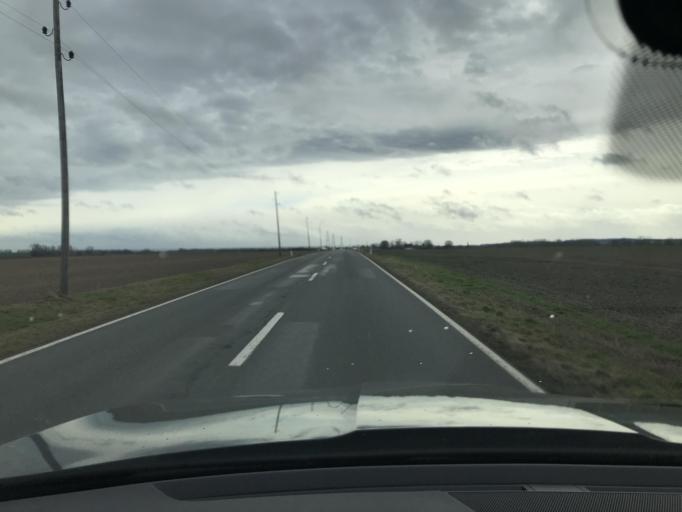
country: DE
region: Saxony-Anhalt
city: Wegeleben
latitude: 51.9127
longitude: 11.1914
